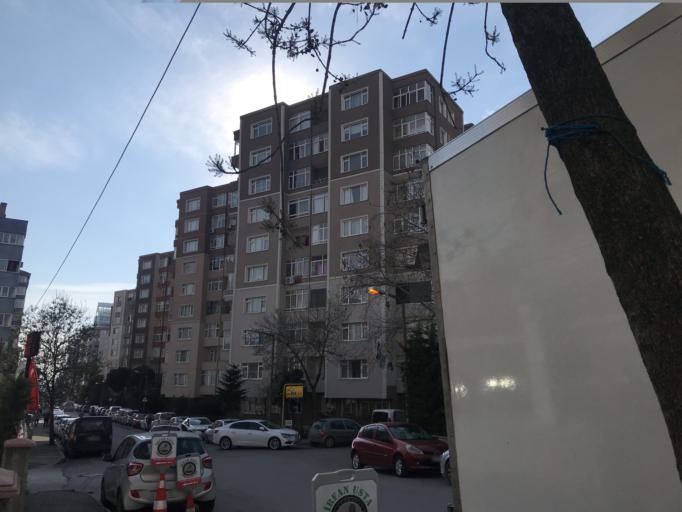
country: TR
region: Istanbul
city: Maltepe
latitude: 40.9403
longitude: 29.1400
